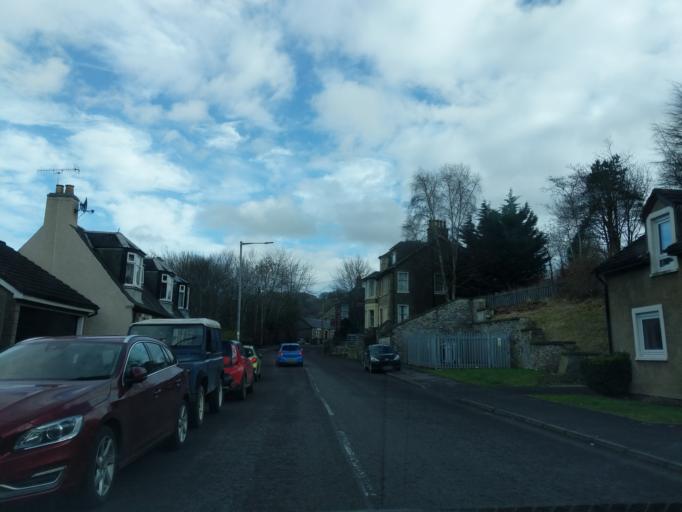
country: GB
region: Scotland
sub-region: South Lanarkshire
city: Lanark
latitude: 55.6752
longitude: -3.8059
